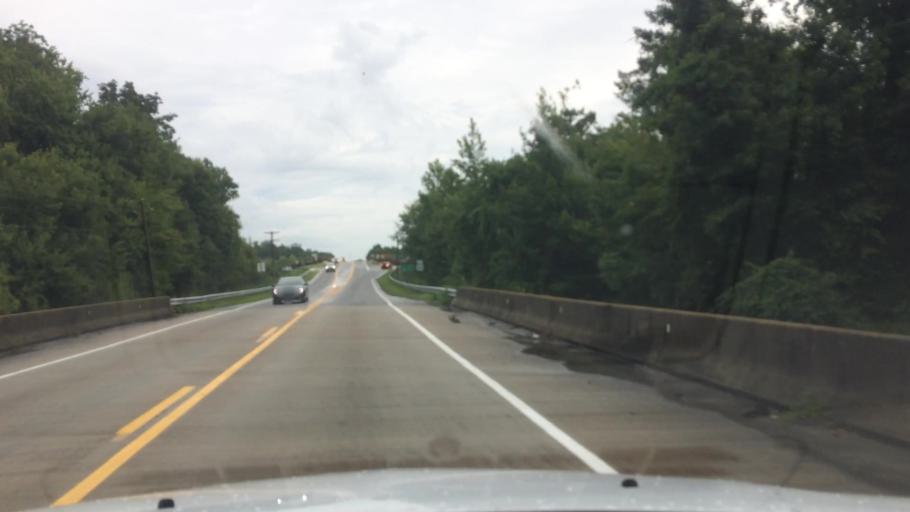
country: US
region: North Carolina
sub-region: Pitt County
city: Farmville
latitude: 35.5956
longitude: -77.5579
